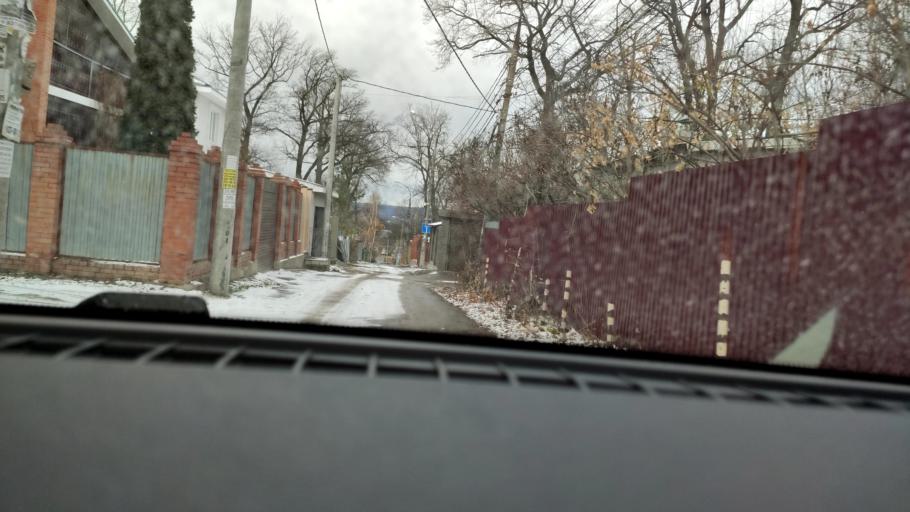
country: RU
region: Samara
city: Samara
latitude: 53.2733
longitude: 50.1989
